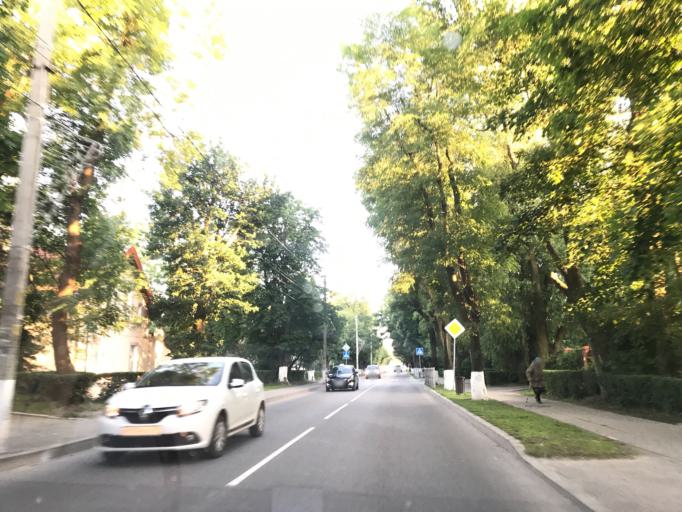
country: RU
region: Kaliningrad
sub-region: Zelenogradskiy Rayon
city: Zelenogradsk
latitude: 54.9567
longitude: 20.4714
